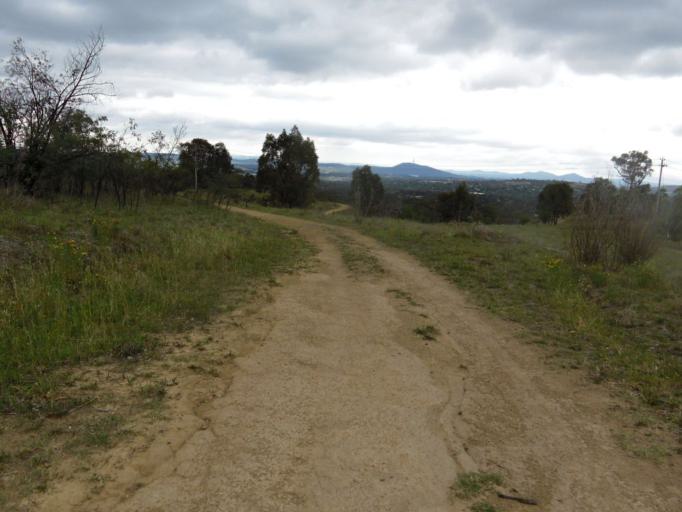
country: AU
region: Australian Capital Territory
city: Macarthur
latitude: -35.3638
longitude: 149.0386
